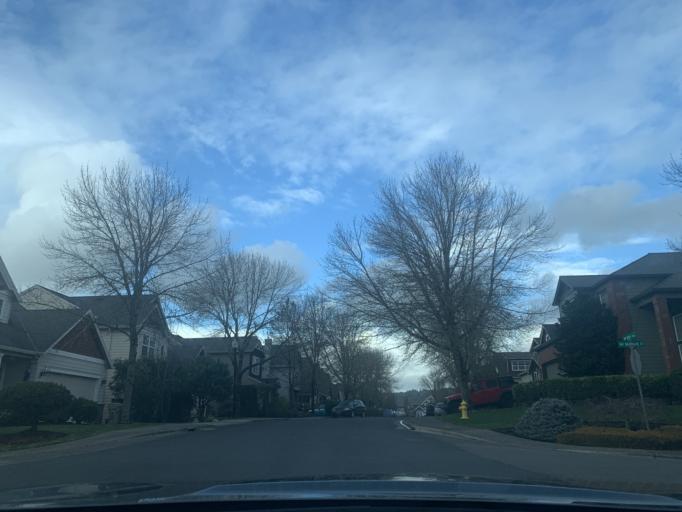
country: US
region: Oregon
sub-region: Washington County
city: Cedar Mill
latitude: 45.5490
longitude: -122.8072
